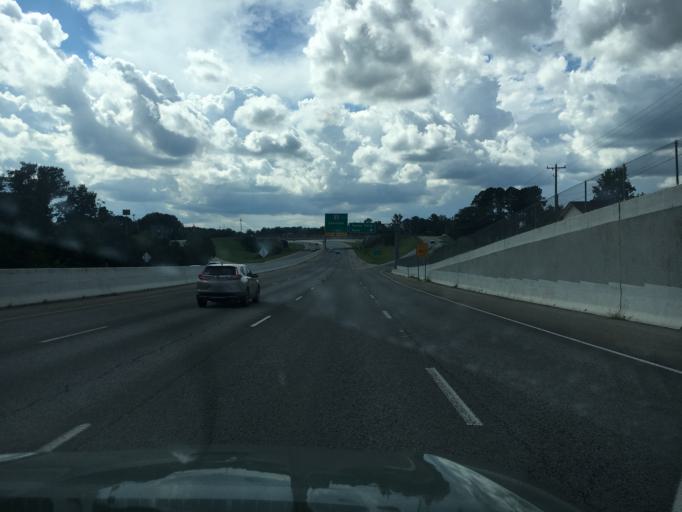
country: US
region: South Carolina
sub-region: Spartanburg County
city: Valley Falls
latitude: 34.9950
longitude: -81.9742
